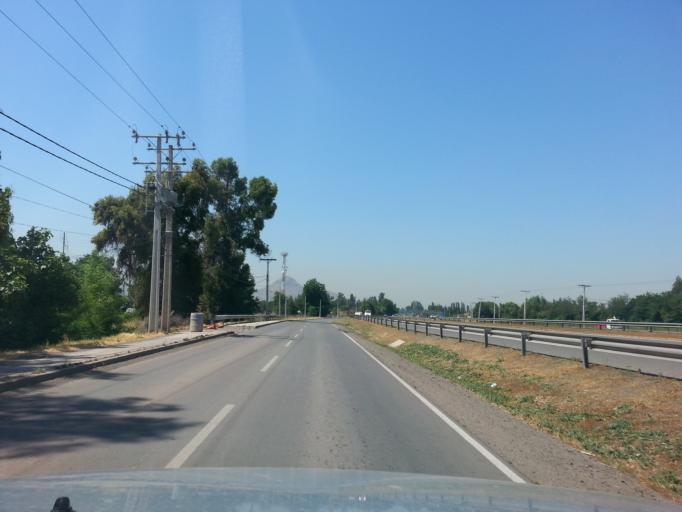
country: CL
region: Santiago Metropolitan
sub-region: Provincia de Chacabuco
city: Chicureo Abajo
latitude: -33.2545
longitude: -70.6977
